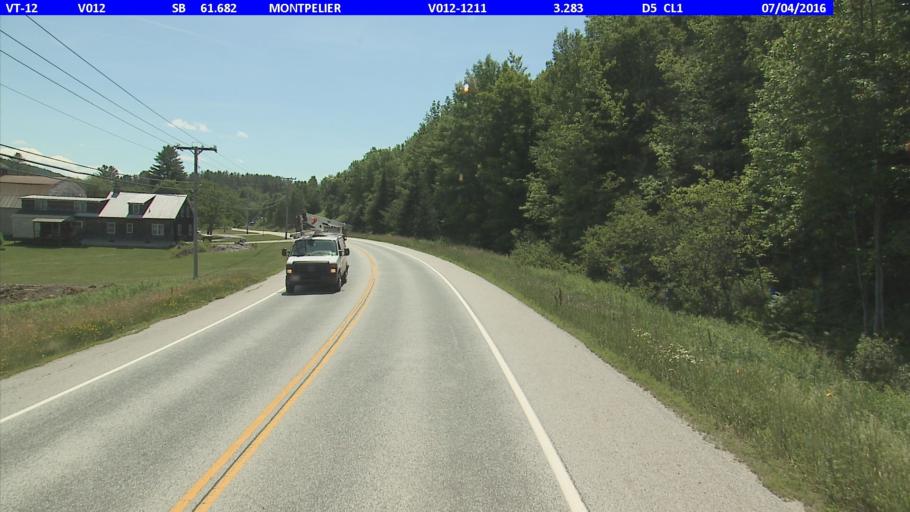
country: US
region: Vermont
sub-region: Washington County
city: Montpelier
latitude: 44.2891
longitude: -72.5792
